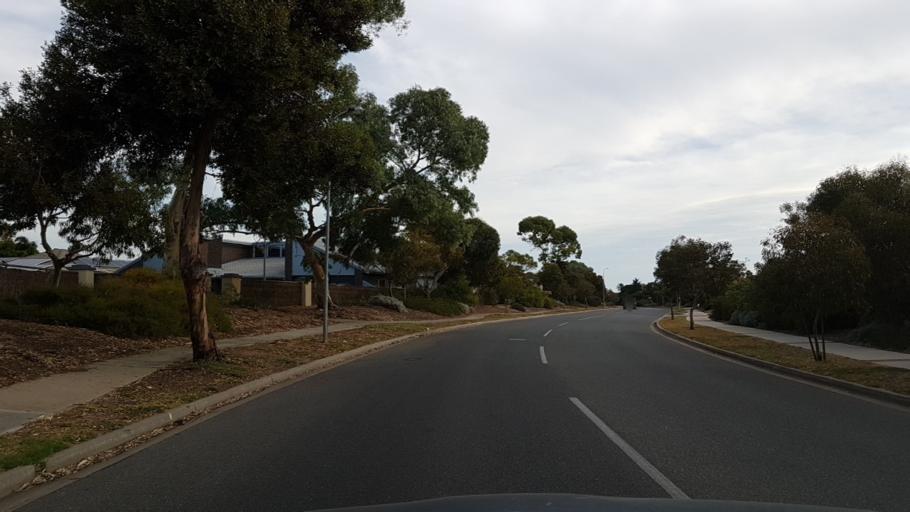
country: AU
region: South Australia
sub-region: Charles Sturt
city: West Lakes Shore
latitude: -34.8625
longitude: 138.4963
